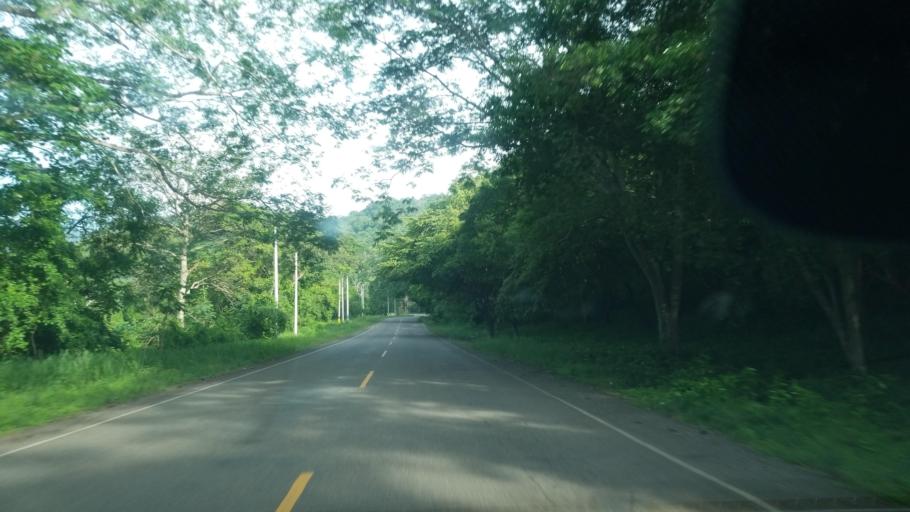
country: HN
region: Santa Barbara
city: Trinidad
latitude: 15.1286
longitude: -88.2105
